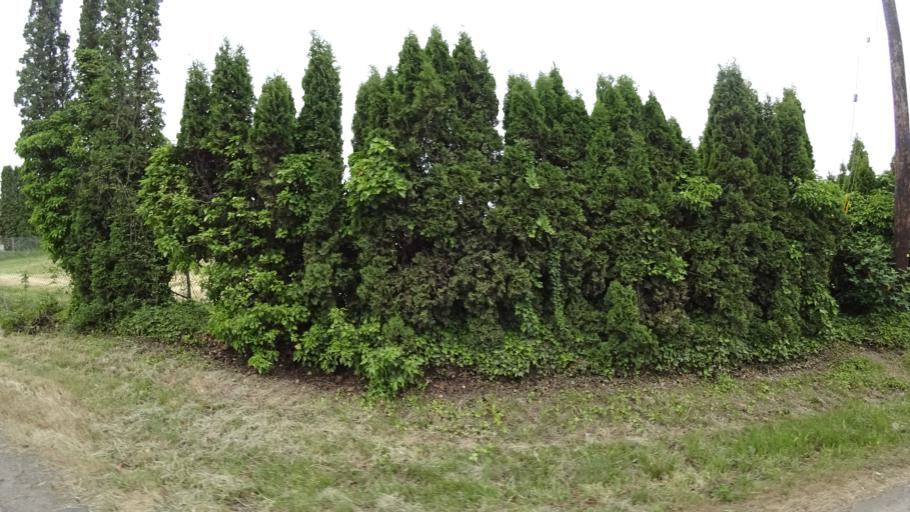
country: US
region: Oregon
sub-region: Washington County
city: Hillsboro
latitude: 45.4955
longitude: -122.9689
